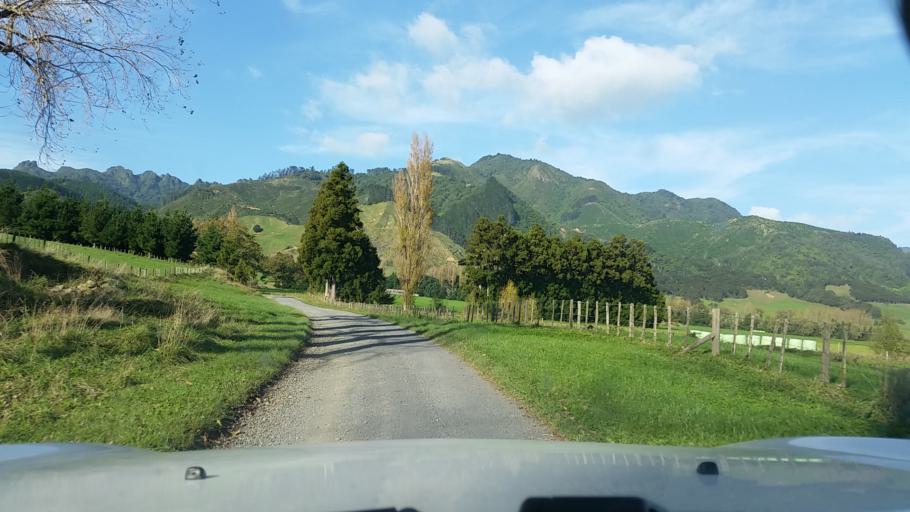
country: NZ
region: Bay of Plenty
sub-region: Western Bay of Plenty District
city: Katikati
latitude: -37.6159
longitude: 175.7994
